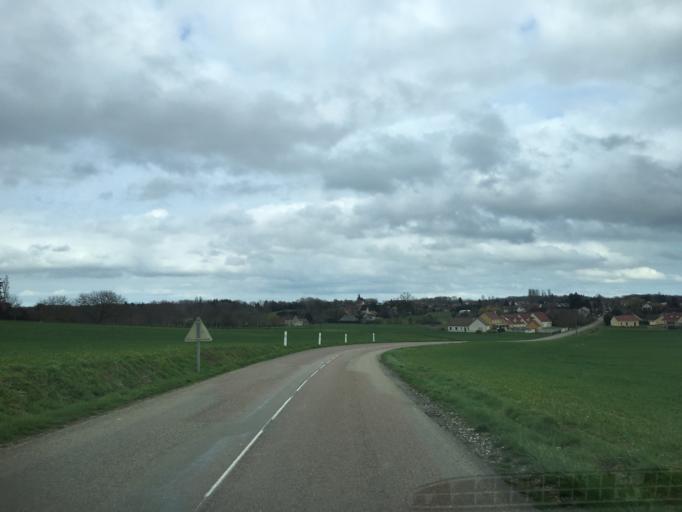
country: FR
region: Bourgogne
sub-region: Departement de l'Yonne
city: Charbuy
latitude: 47.8000
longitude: 3.4284
